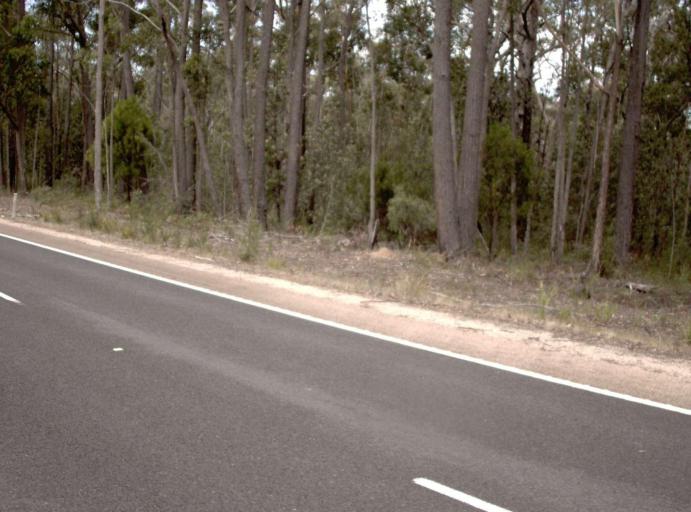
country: AU
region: New South Wales
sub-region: Bega Valley
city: Eden
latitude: -37.5045
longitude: 149.5334
